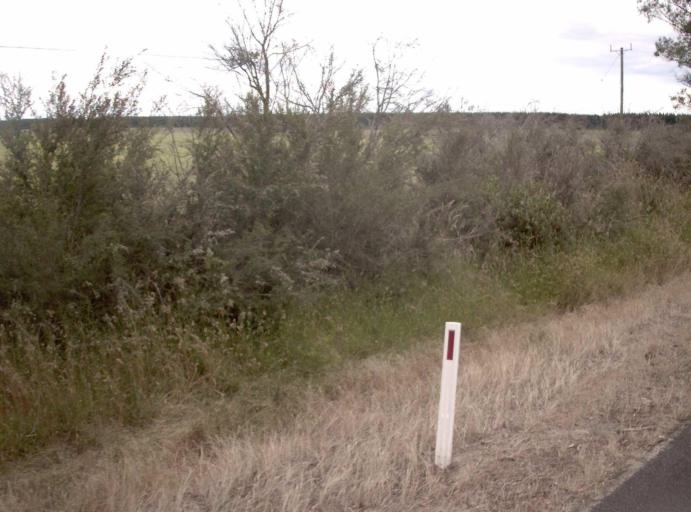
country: AU
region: Victoria
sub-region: Wellington
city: Sale
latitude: -38.2273
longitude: 147.0553
